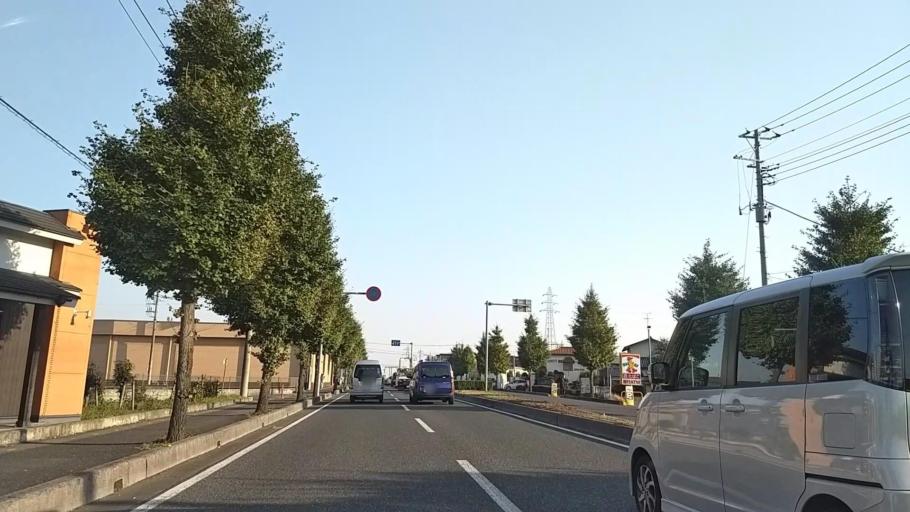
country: JP
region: Saitama
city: Sayama
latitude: 35.8072
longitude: 139.4067
